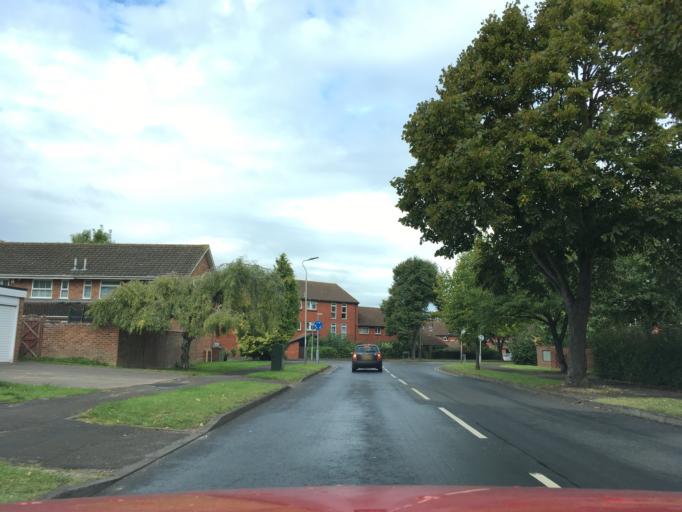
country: GB
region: England
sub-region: Gloucestershire
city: Uckington
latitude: 51.9029
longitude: -2.1241
